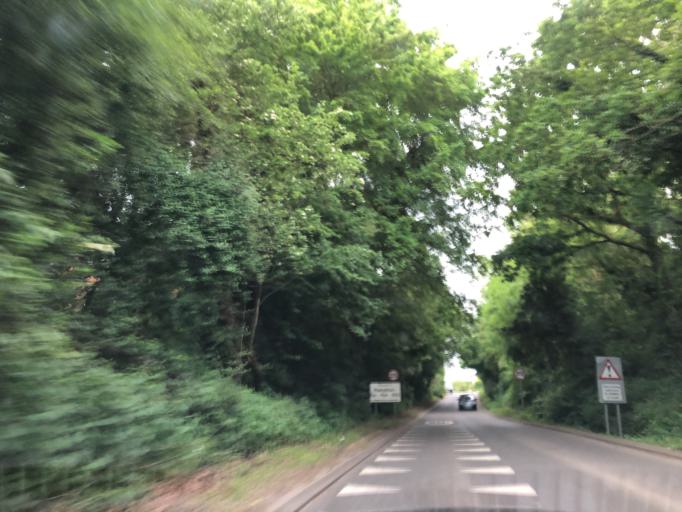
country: GB
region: England
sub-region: Warwickshire
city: Warwick
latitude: 52.2799
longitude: -1.6317
